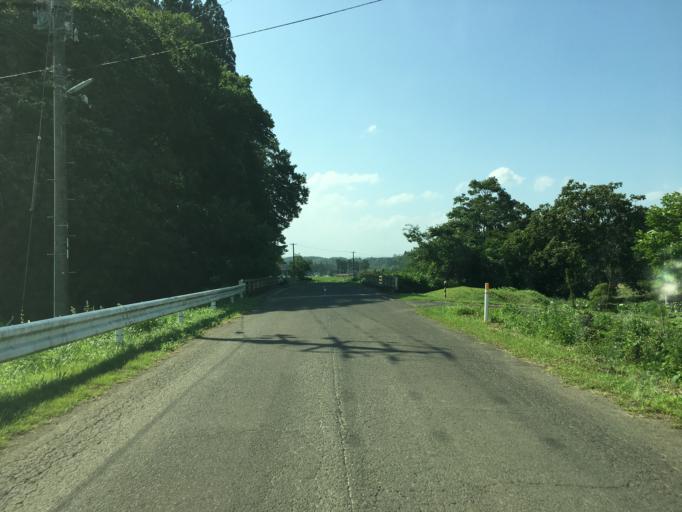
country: JP
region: Miyagi
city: Marumori
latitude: 37.8897
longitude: 140.8371
